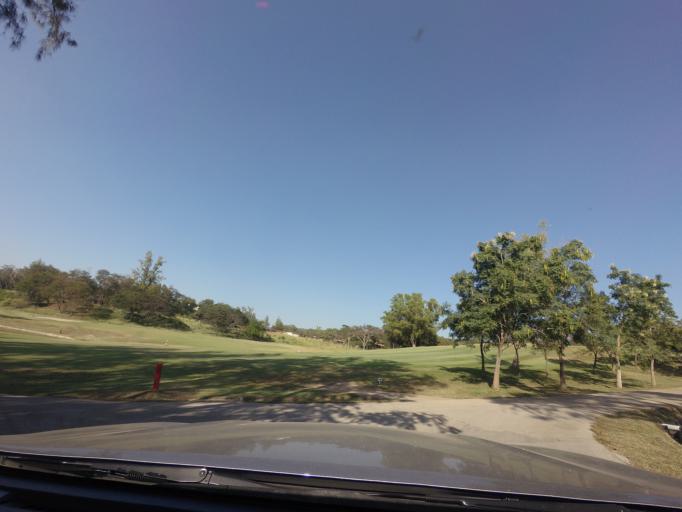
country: TH
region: Lampang
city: Mae Mo
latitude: 18.3234
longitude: 99.7447
